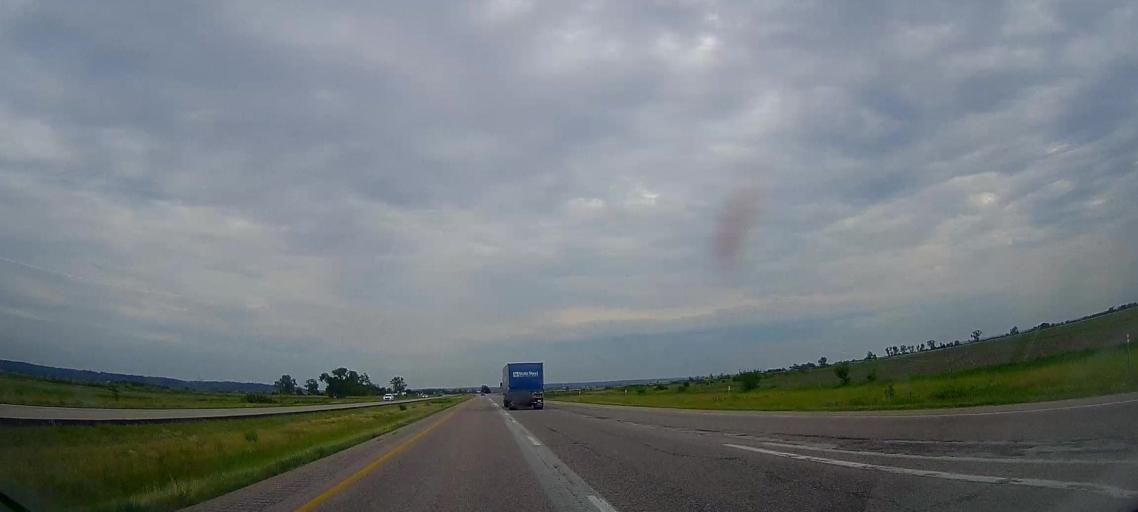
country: US
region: Iowa
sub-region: Harrison County
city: Missouri Valley
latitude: 41.5896
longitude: -95.9502
